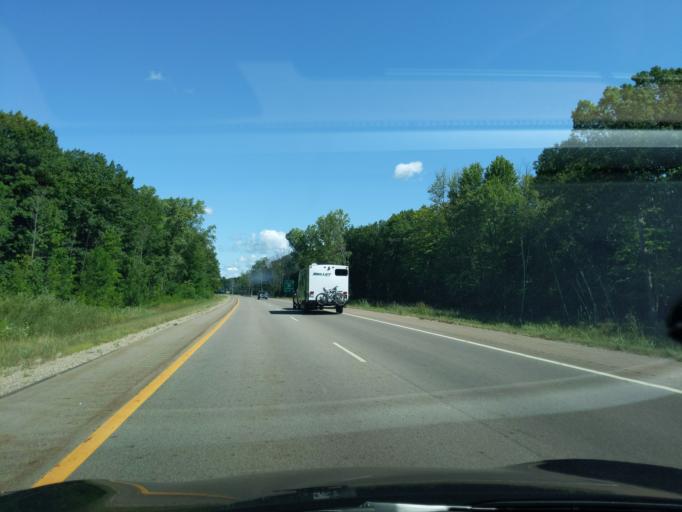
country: US
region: Michigan
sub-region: Gratiot County
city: Saint Louis
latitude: 43.3657
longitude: -84.6004
